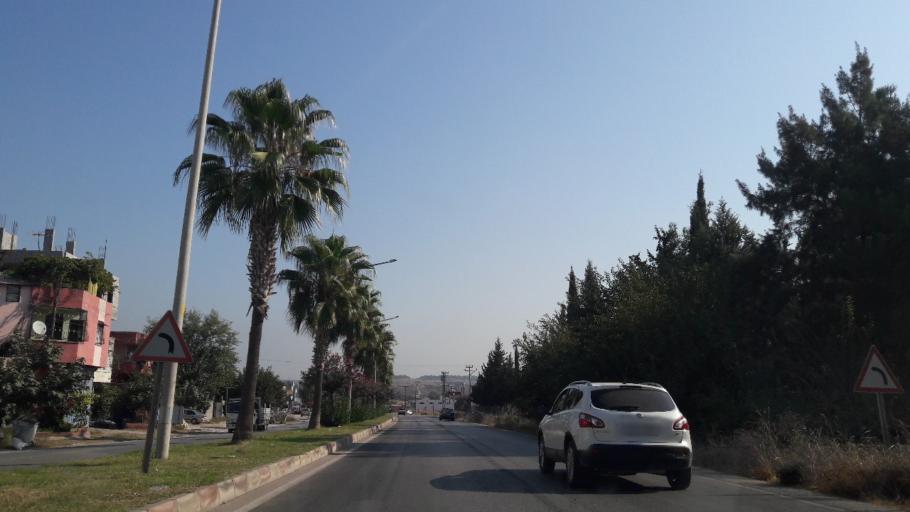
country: TR
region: Adana
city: Yuregir
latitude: 37.0445
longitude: 35.4338
